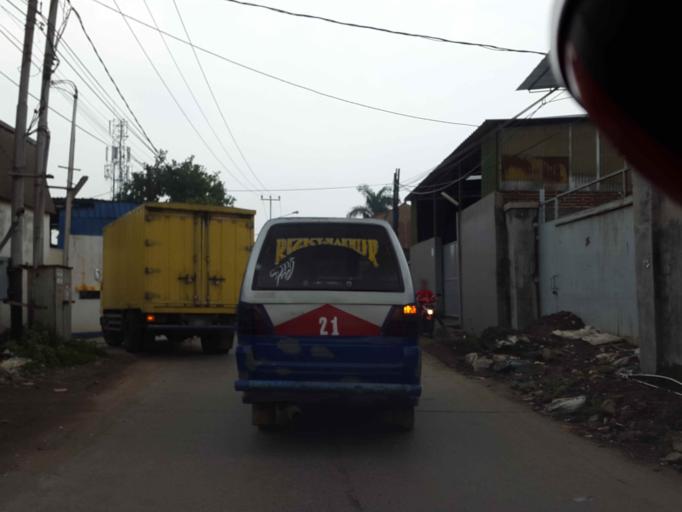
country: ID
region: West Java
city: Cimahi
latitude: -6.9049
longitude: 107.5538
